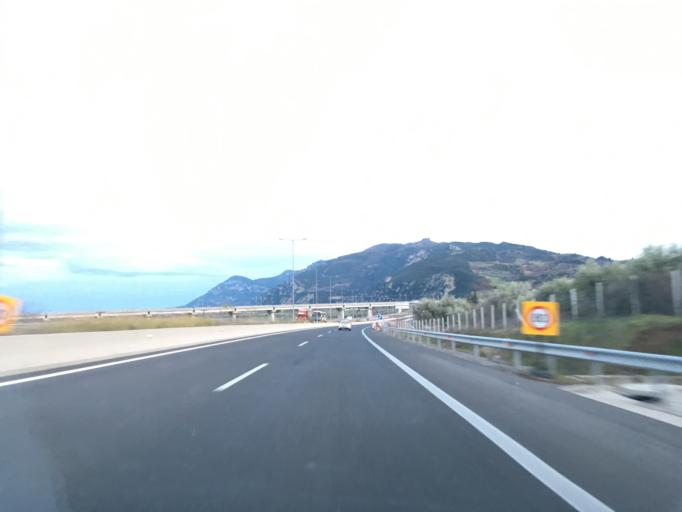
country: GR
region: Central Greece
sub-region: Nomos Fthiotidos
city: Kainouryion
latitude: 38.7870
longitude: 22.6967
